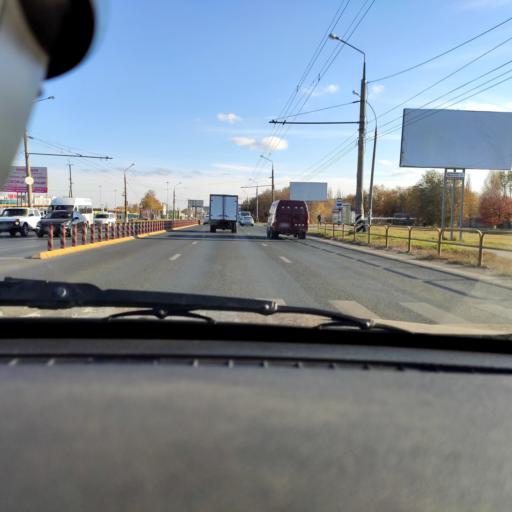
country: RU
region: Samara
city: Tol'yatti
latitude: 53.5432
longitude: 49.3833
